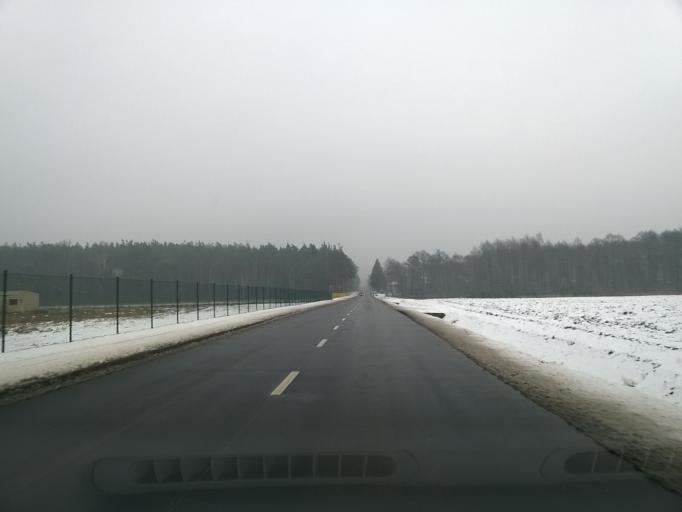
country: PL
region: Kujawsko-Pomorskie
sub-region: Powiat swiecki
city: Swiecie
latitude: 53.4175
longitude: 18.3840
